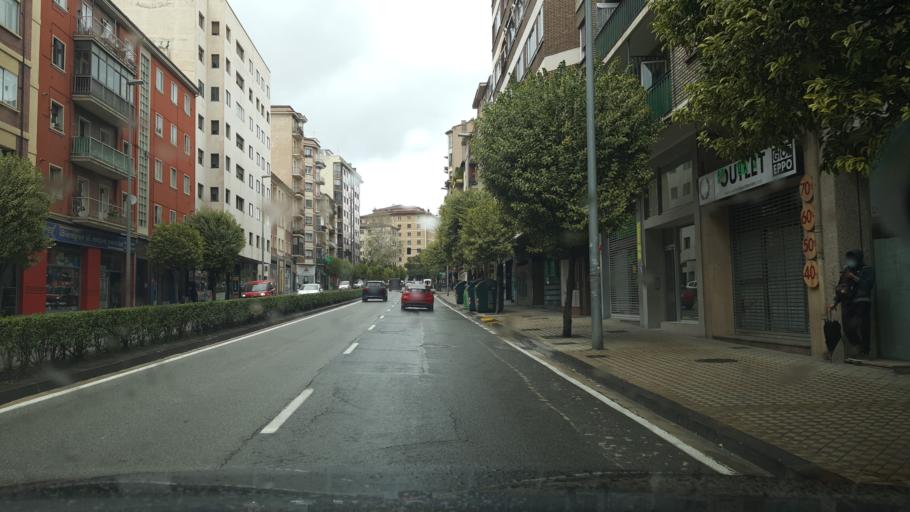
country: ES
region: Navarre
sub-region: Provincia de Navarra
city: Segundo Ensanche
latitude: 42.8029
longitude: -1.6440
